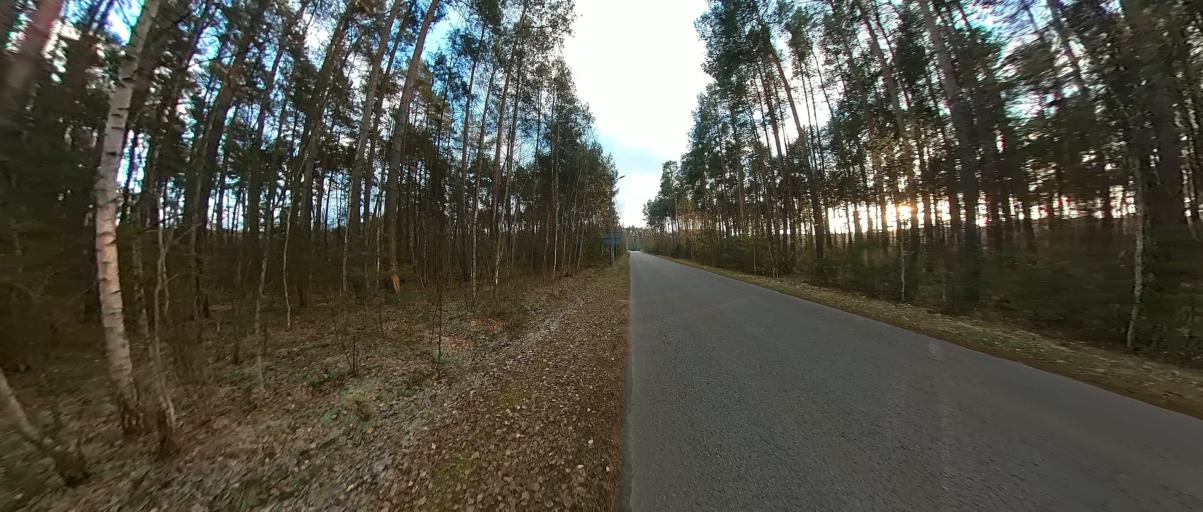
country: PL
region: Masovian Voivodeship
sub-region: Powiat bialobrzeski
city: Bialobrzegi
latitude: 51.6511
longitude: 20.9747
